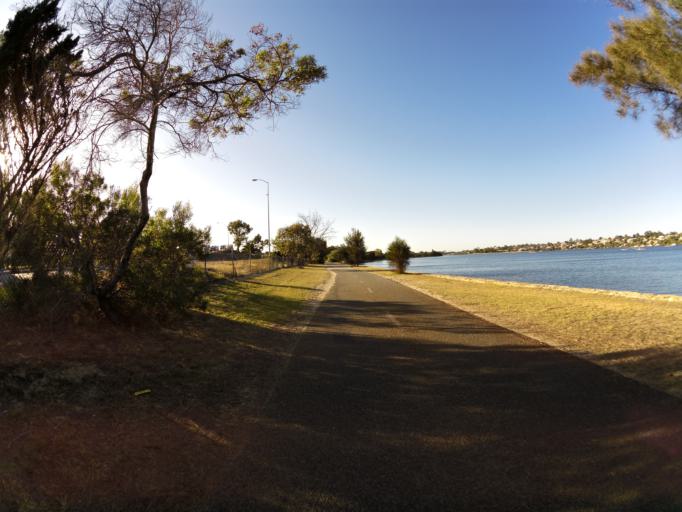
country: AU
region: Western Australia
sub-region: South Perth
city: Manning
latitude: -32.0122
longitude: 115.8564
